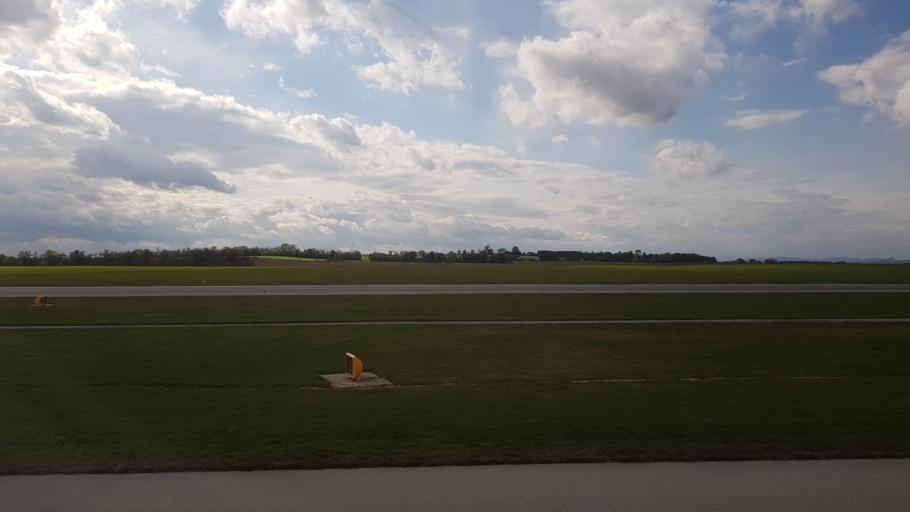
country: AT
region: Lower Austria
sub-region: Politischer Bezirk Bruck an der Leitha
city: Enzersdorf an der Fischa
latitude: 48.1059
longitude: 16.5810
